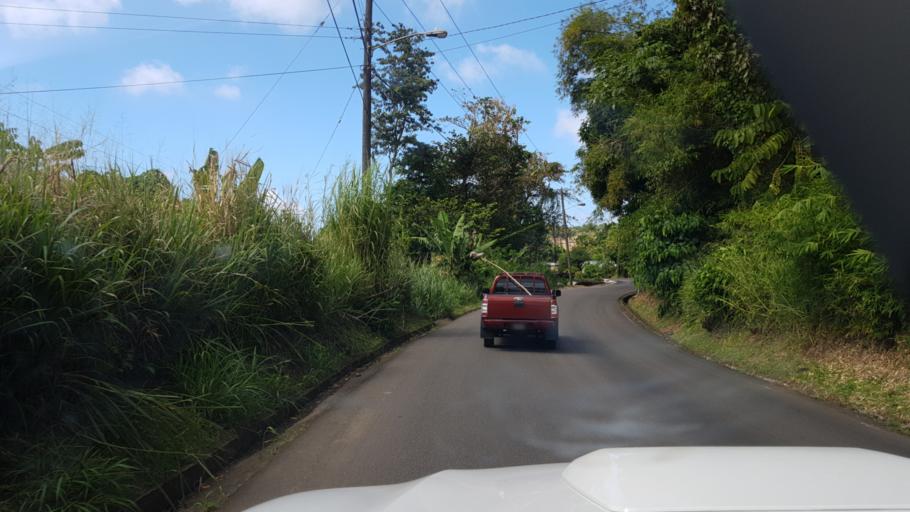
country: LC
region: Castries Quarter
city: Bisee
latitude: 14.0190
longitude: -60.9595
